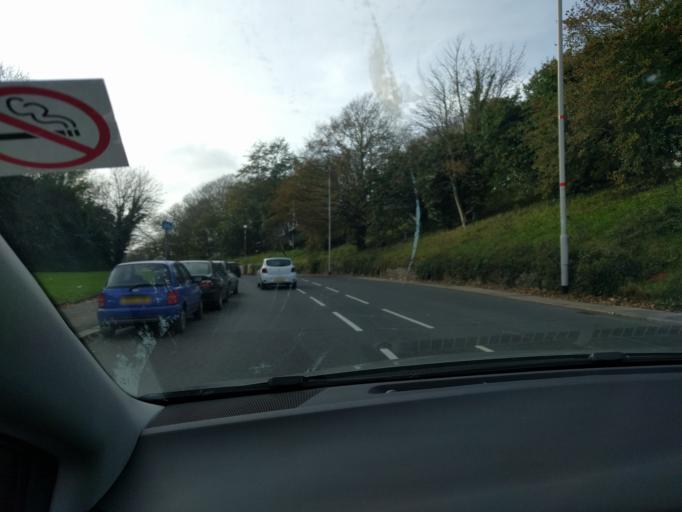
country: GB
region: England
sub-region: Cornwall
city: Millbrook
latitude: 50.3697
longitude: -4.1665
